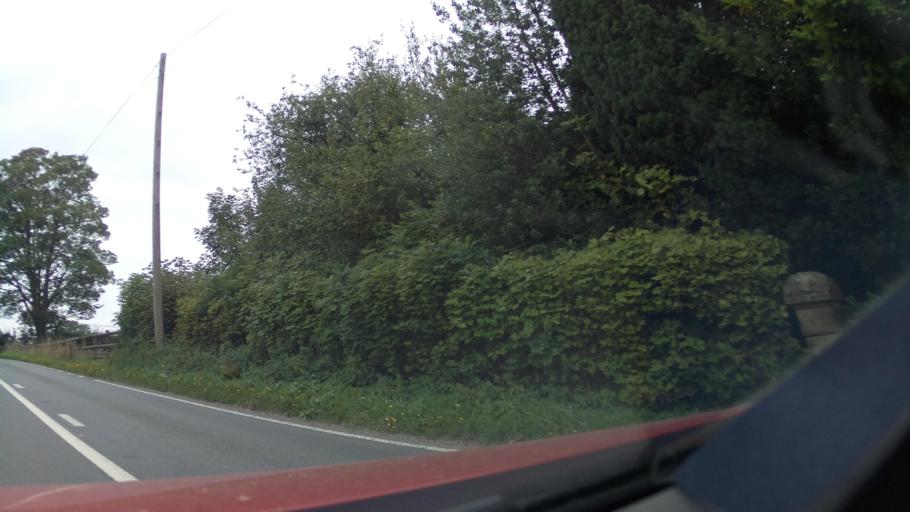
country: GB
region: England
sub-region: Derbyshire
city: Wirksworth
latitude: 53.0192
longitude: -1.5985
